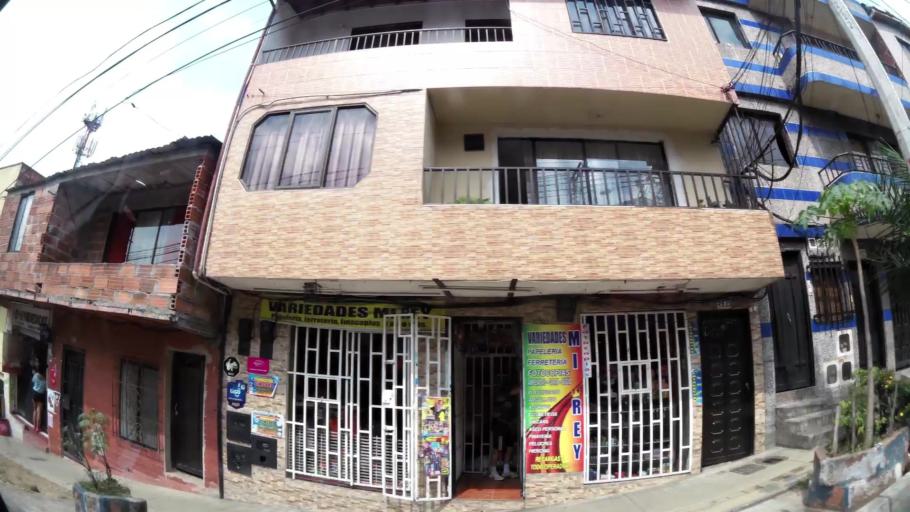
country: CO
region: Antioquia
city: Medellin
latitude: 6.2729
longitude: -75.5581
